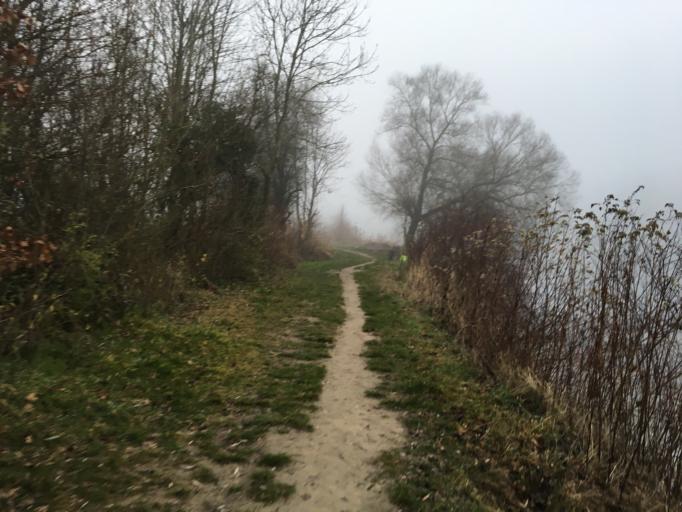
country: CH
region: Aargau
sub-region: Bezirk Zurzach
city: Bad Zurzach
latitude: 47.5912
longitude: 8.2978
